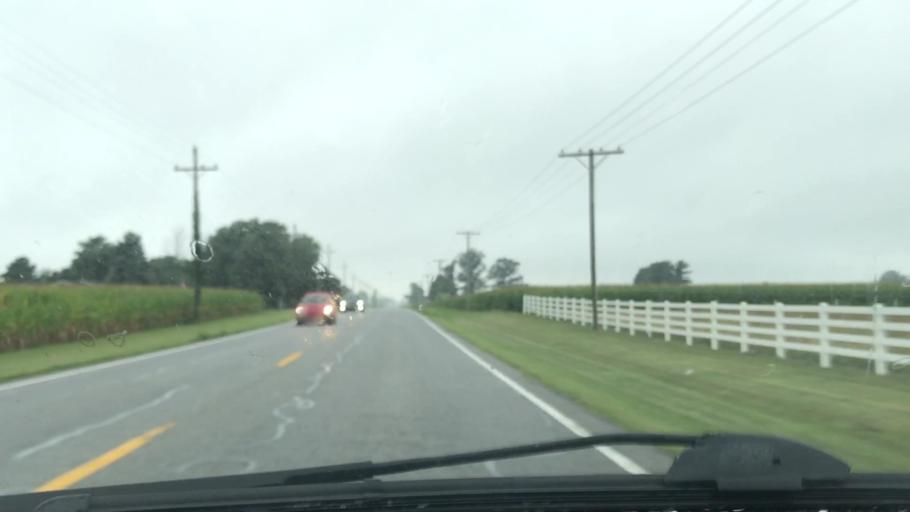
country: US
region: Indiana
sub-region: Hamilton County
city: Sheridan
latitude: 40.1285
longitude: -86.3039
